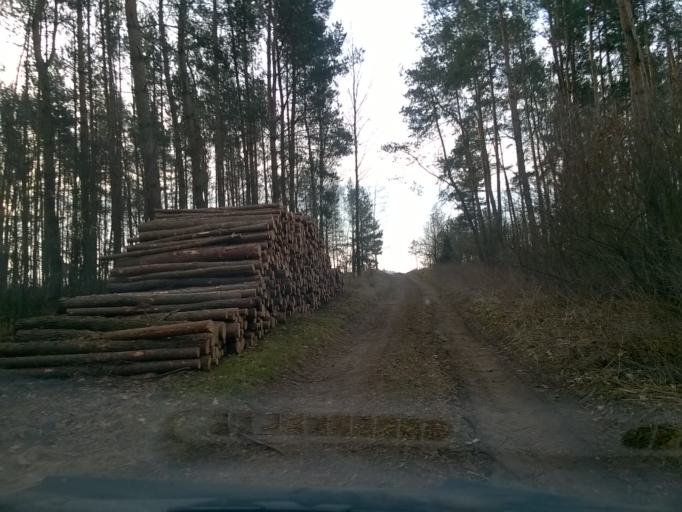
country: PL
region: Kujawsko-Pomorskie
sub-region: Powiat tucholski
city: Kesowo
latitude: 53.5512
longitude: 17.6795
